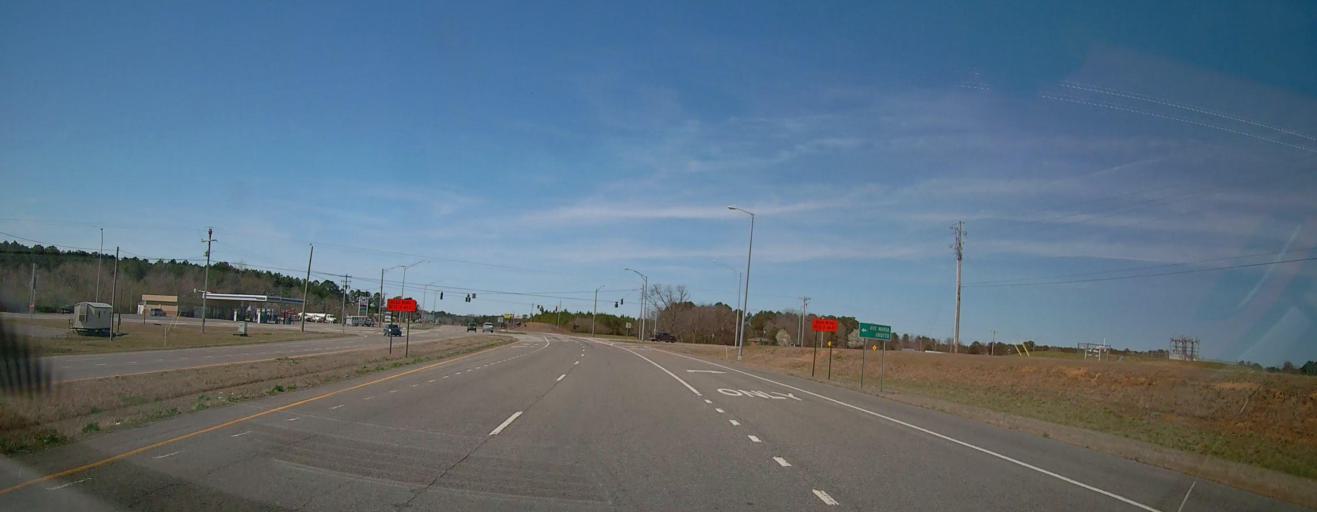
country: US
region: Alabama
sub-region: Cullman County
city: Cullman
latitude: 34.1912
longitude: -86.7854
